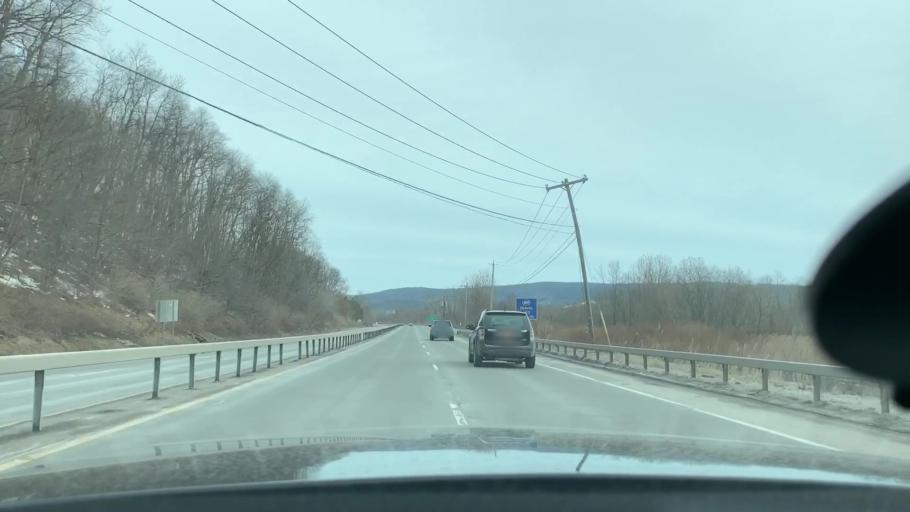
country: US
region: New York
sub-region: Herkimer County
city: Ilion
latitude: 43.0190
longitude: -75.0213
